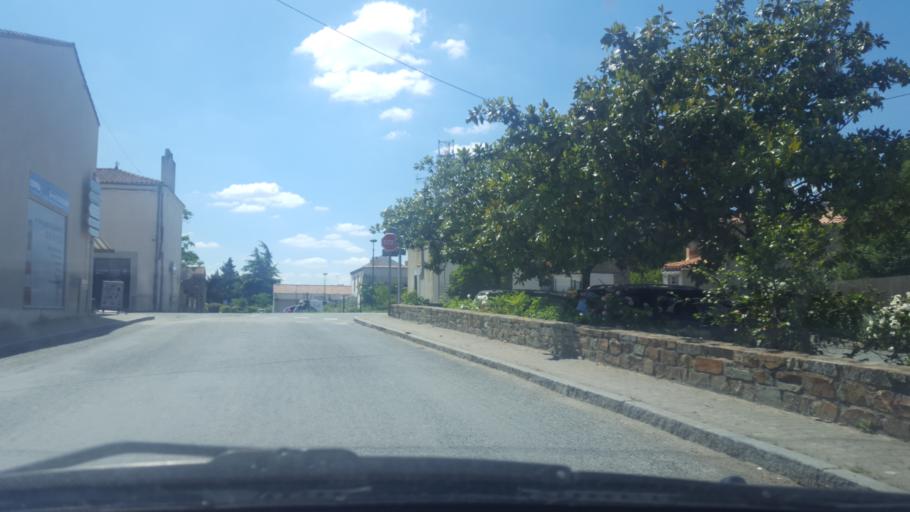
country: FR
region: Pays de la Loire
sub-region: Departement de la Vendee
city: Saint-Philbert-de-Bouaine
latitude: 46.9841
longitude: -1.5206
